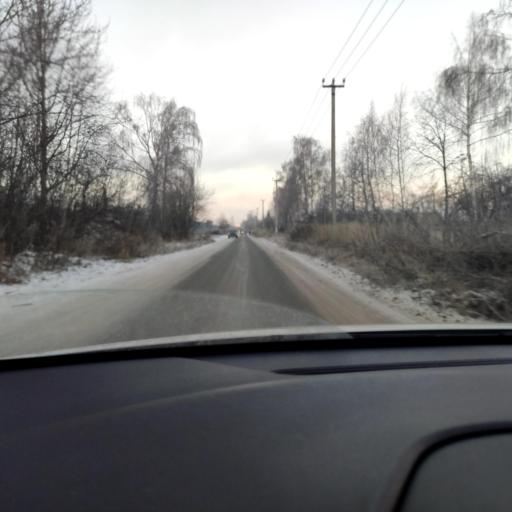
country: RU
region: Tatarstan
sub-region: Gorod Kazan'
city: Kazan
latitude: 55.8603
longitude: 49.0546
